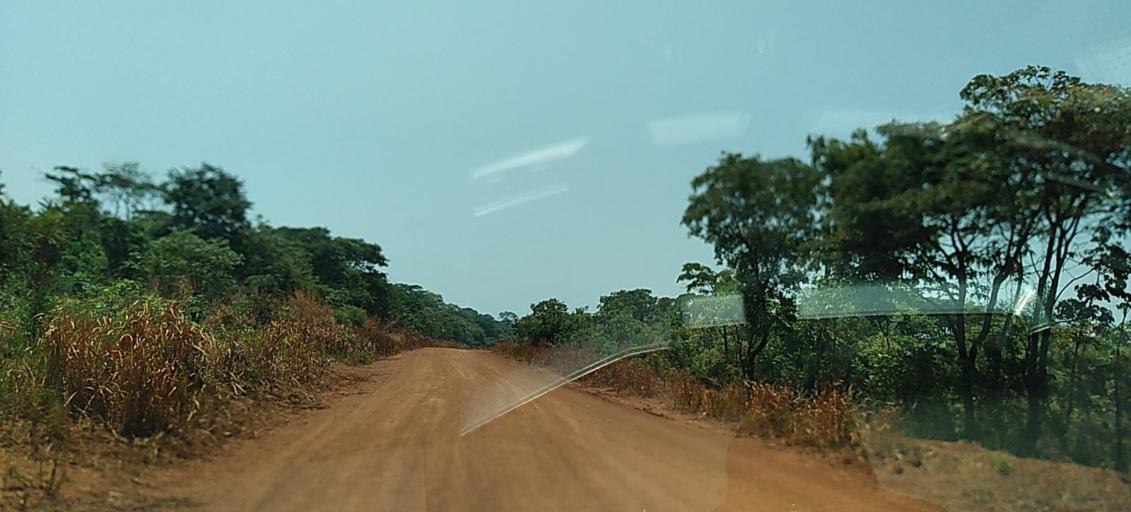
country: CD
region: Katanga
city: Kipushi
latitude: -11.9836
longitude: 26.8625
